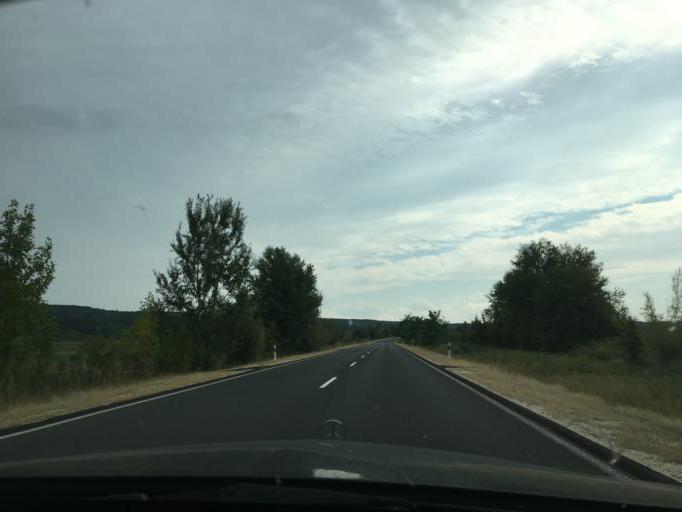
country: HU
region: Somogy
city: Balatonszarszo
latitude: 46.8288
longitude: 17.8508
